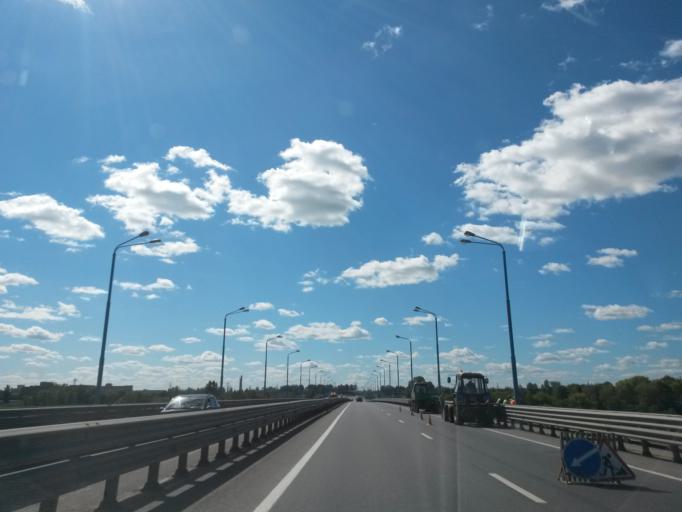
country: RU
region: Jaroslavl
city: Yaroslavl
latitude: 57.6738
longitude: 39.8539
